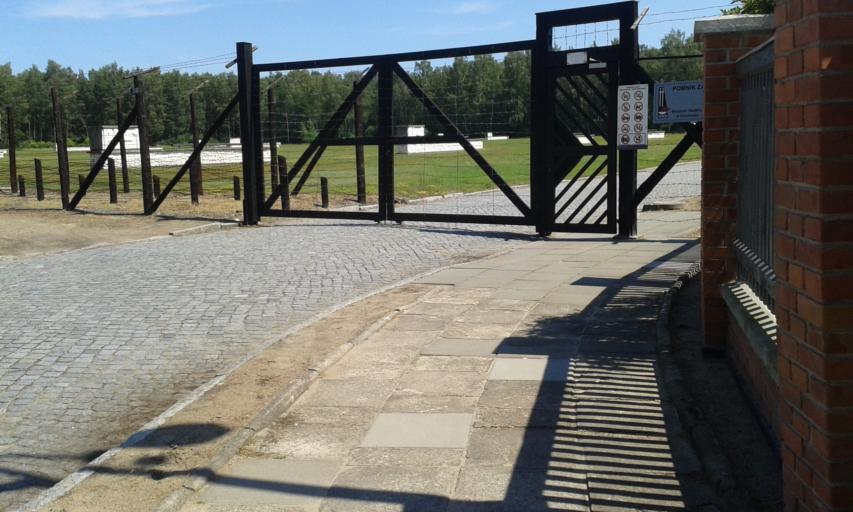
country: PL
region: Pomeranian Voivodeship
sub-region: Powiat nowodworski
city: Sztutowo
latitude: 54.3289
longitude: 19.1543
